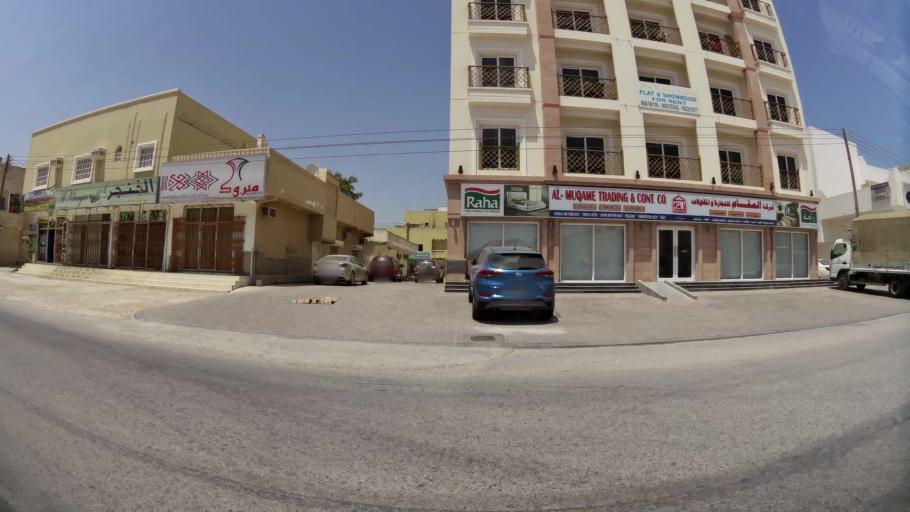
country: OM
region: Zufar
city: Salalah
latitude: 17.0121
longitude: 54.0795
